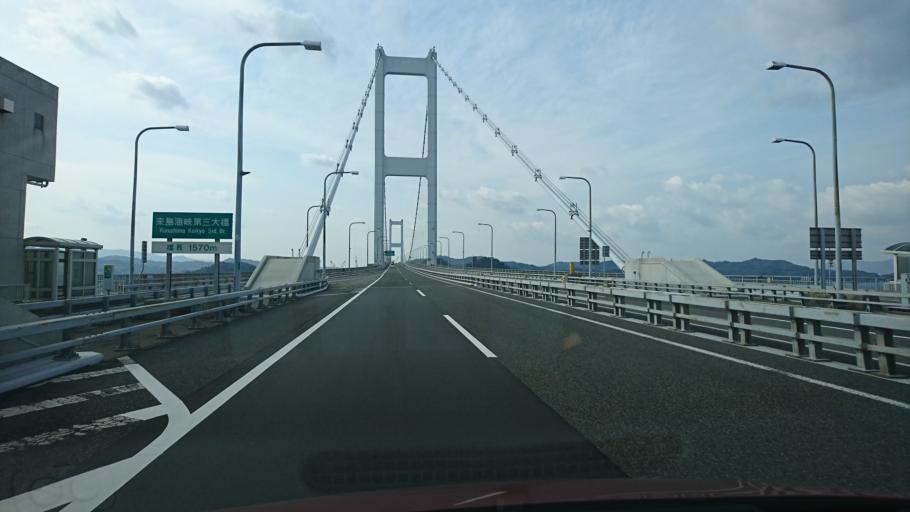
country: JP
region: Hiroshima
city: Takehara
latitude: 34.1182
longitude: 132.9926
